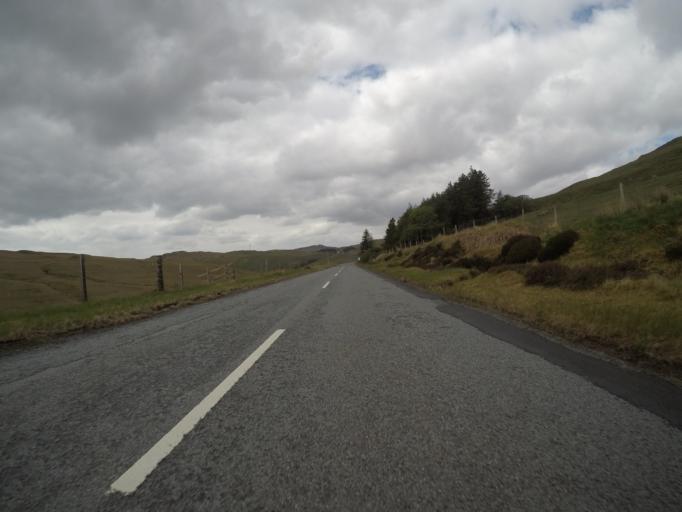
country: GB
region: Scotland
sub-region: Highland
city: Isle of Skye
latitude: 57.3231
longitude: -6.3300
